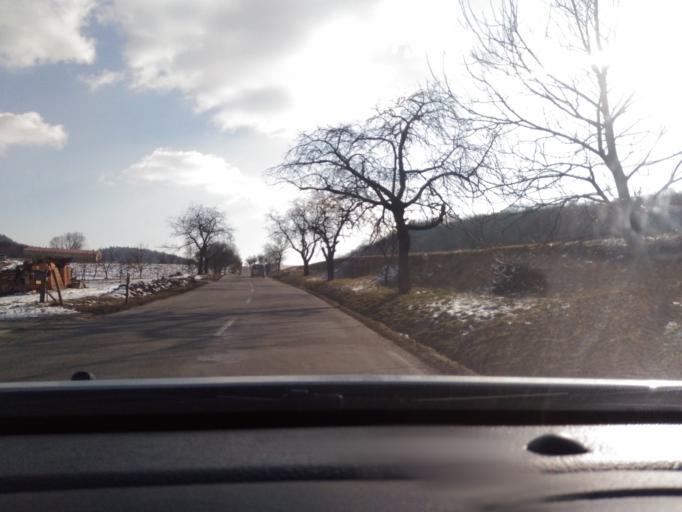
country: CZ
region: South Moravian
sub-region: Okres Brno-Venkov
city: Nedvedice
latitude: 49.4170
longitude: 16.3517
